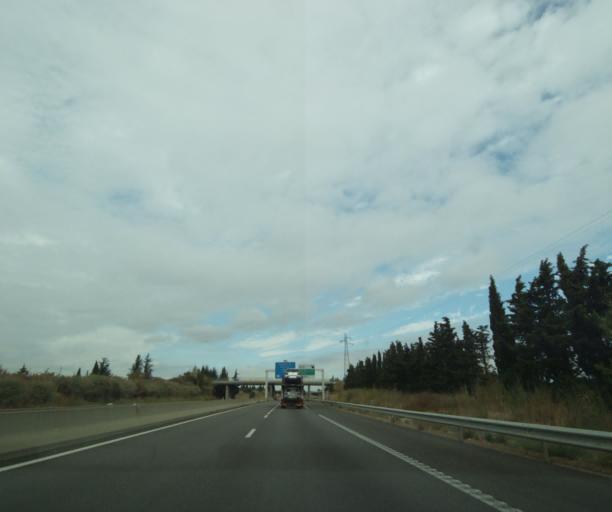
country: FR
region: Provence-Alpes-Cote d'Azur
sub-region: Departement des Bouches-du-Rhone
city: Saint-Martin-de-Crau
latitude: 43.6357
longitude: 4.8282
